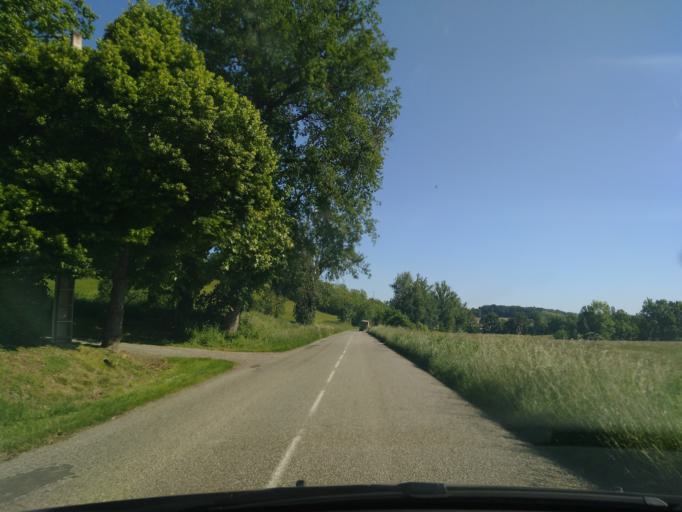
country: FR
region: Midi-Pyrenees
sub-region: Departement du Gers
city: Gimont
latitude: 43.6107
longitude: 0.8536
